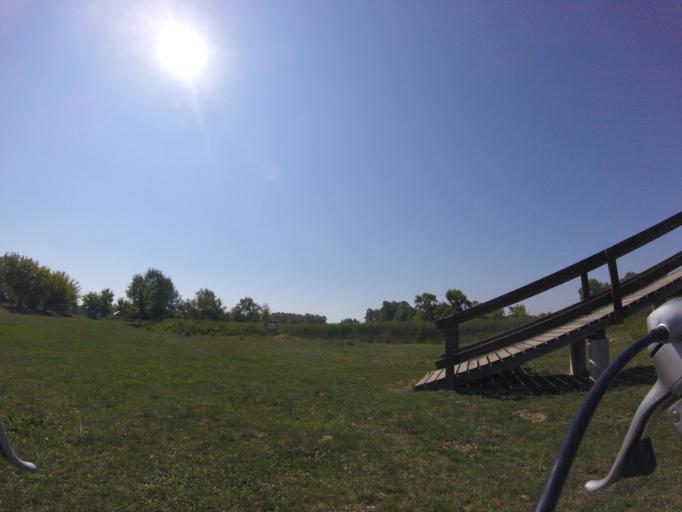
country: HU
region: Szabolcs-Szatmar-Bereg
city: Tiszalok
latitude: 48.0276
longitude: 21.3824
